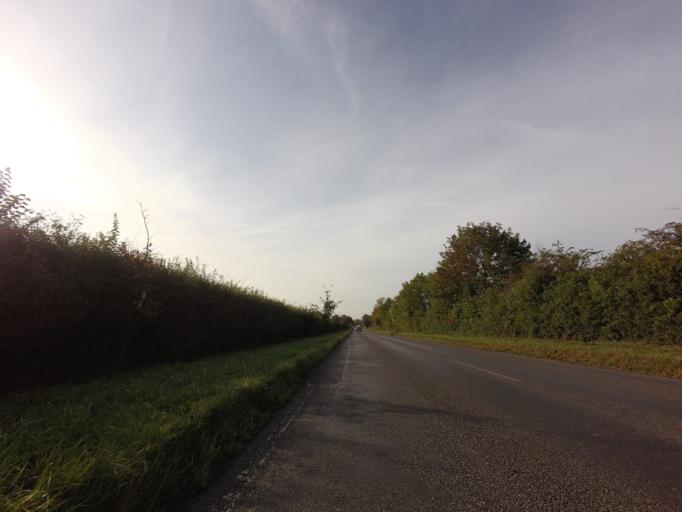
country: GB
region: England
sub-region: Cambridgeshire
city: Harston
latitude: 52.1288
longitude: 0.1001
